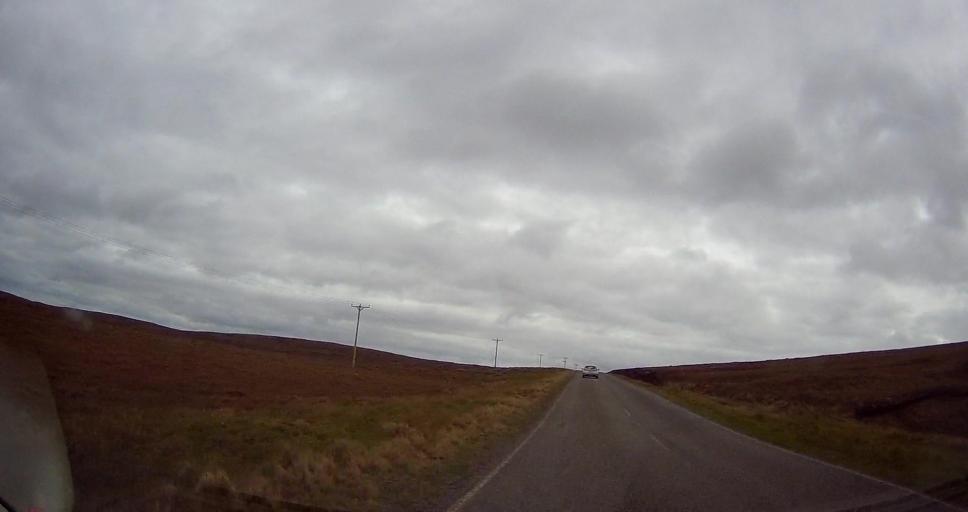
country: GB
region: Scotland
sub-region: Shetland Islands
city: Shetland
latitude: 60.6665
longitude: -1.0176
